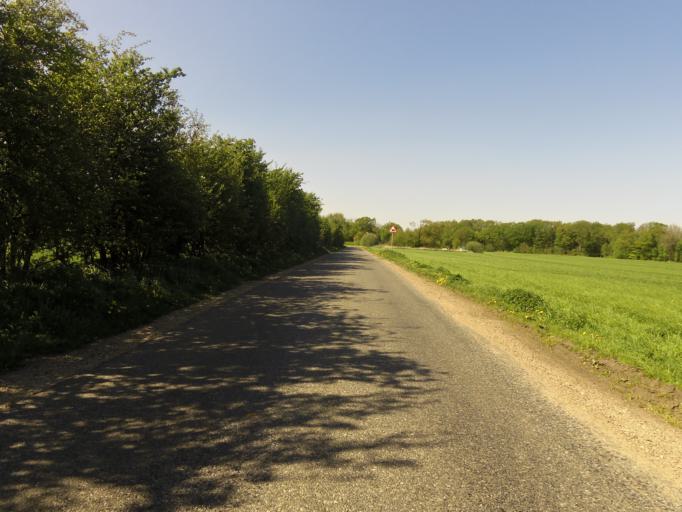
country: DK
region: South Denmark
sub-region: Tonder Kommune
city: Sherrebek
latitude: 55.2179
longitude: 8.8479
